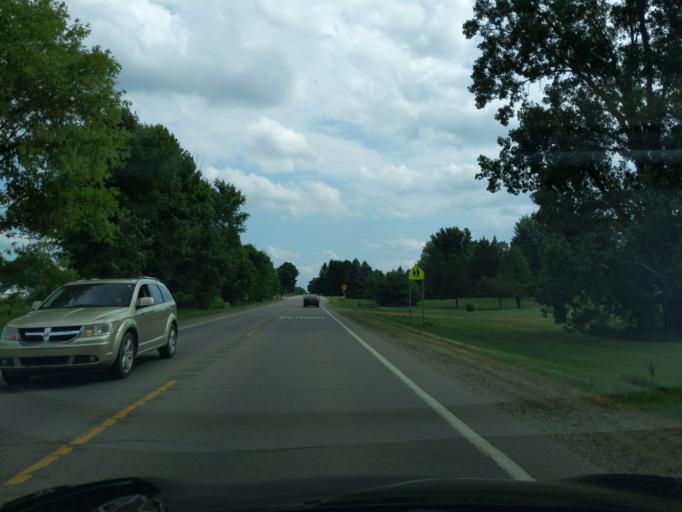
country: US
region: Michigan
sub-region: Eaton County
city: Eaton Rapids
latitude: 42.4760
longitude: -84.6597
